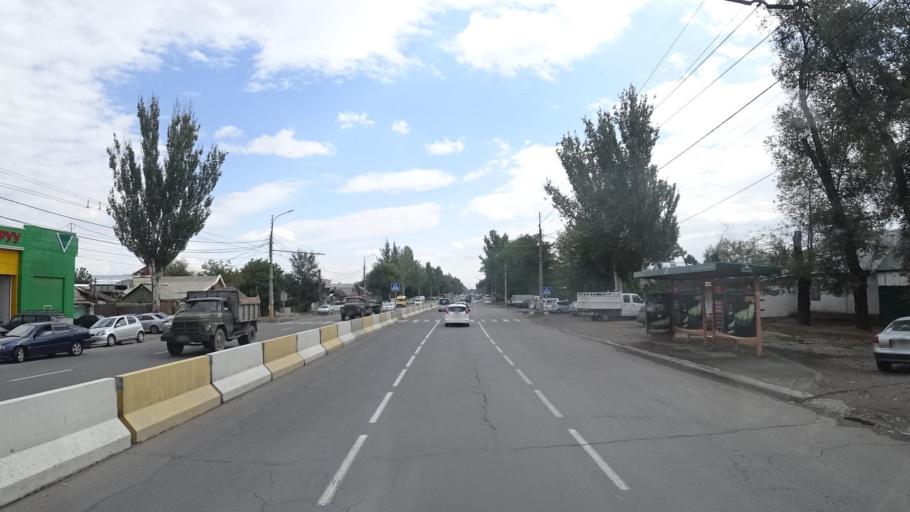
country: KG
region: Chuy
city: Lebedinovka
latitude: 42.8885
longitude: 74.6438
